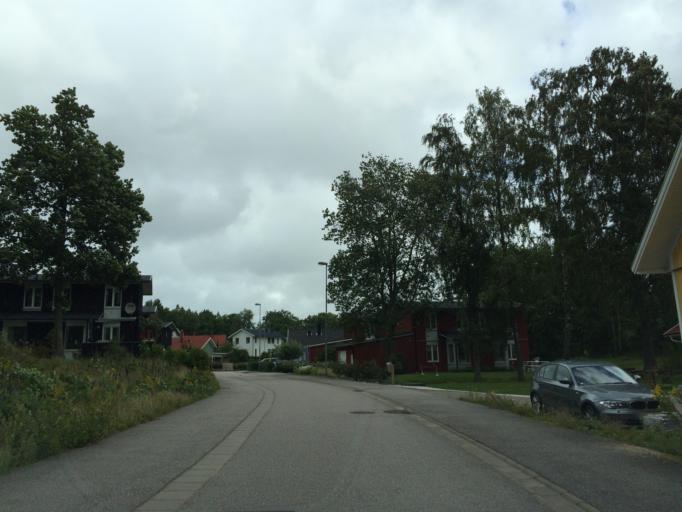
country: SE
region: Vaestra Goetaland
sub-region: Trollhattan
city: Trollhattan
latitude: 58.2889
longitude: 12.2648
